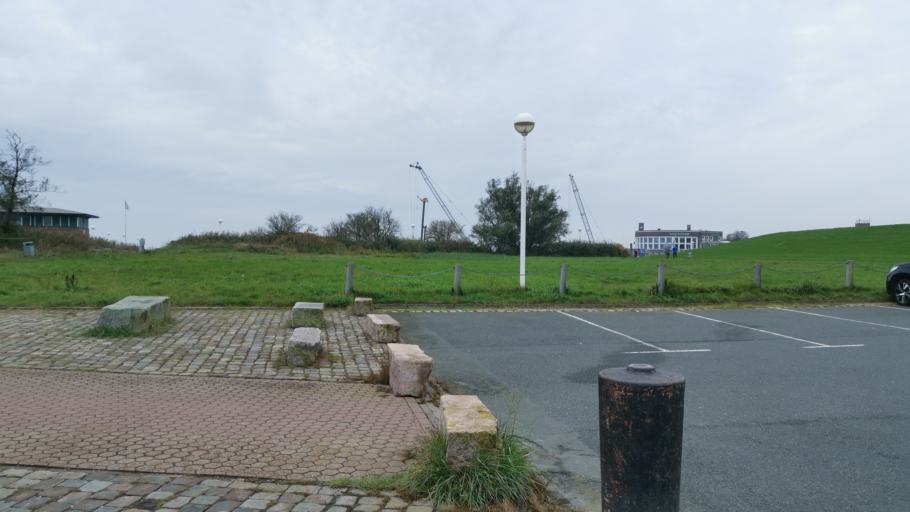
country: DE
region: Lower Saxony
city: Wilhelmshaven
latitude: 53.5148
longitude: 8.1488
